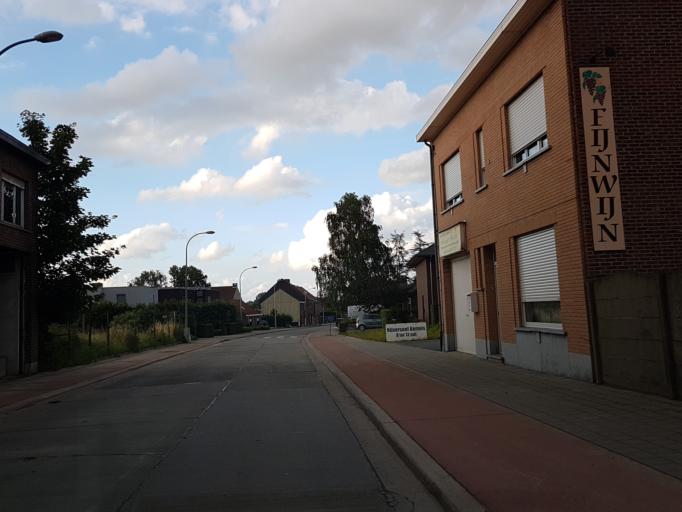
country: BE
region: Flanders
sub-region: Provincie Vlaams-Brabant
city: Opwijk
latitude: 50.9635
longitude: 4.1586
